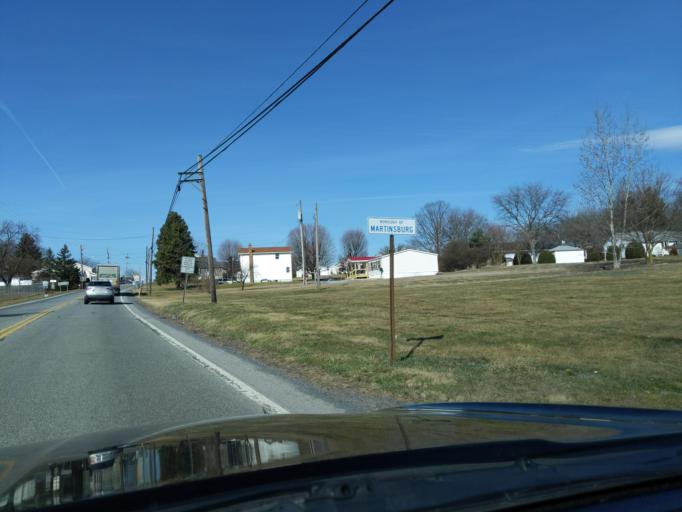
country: US
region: Pennsylvania
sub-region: Blair County
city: Martinsburg
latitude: 40.3091
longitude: -78.3154
